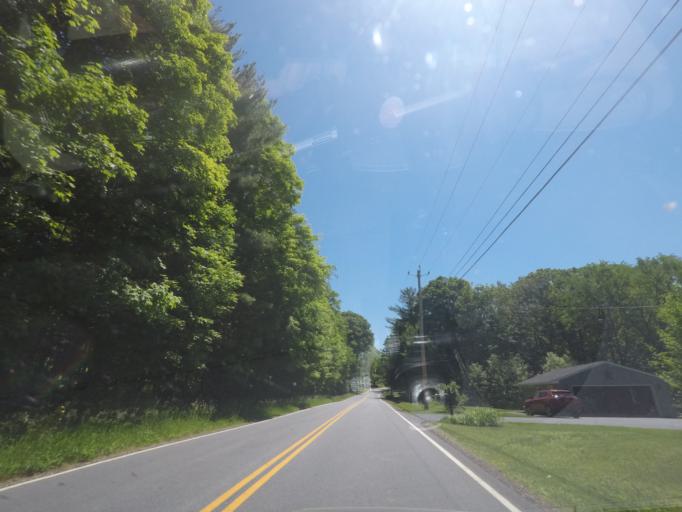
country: US
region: New York
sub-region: Saratoga County
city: Country Knolls
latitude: 42.9459
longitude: -73.7694
